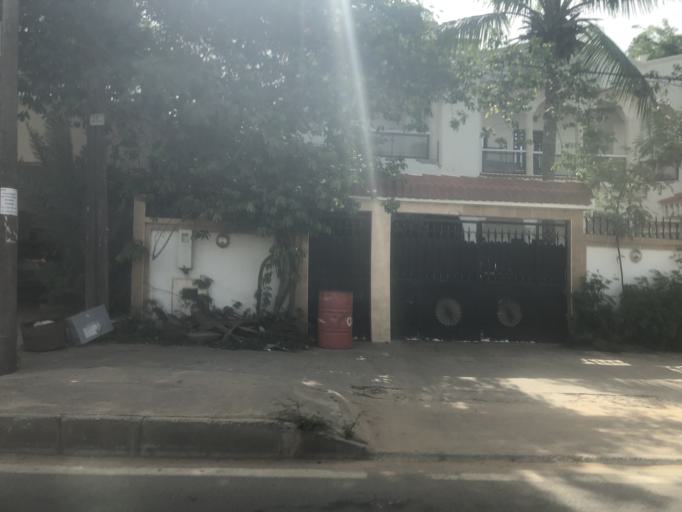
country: SN
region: Dakar
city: Mermoz Boabab
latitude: 14.7394
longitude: -17.5102
